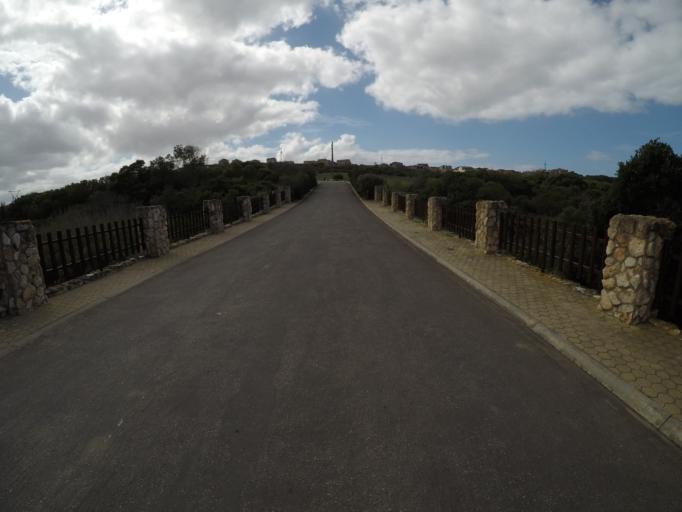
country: ZA
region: Western Cape
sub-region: Eden District Municipality
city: Mossel Bay
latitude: -34.1428
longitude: 22.0890
